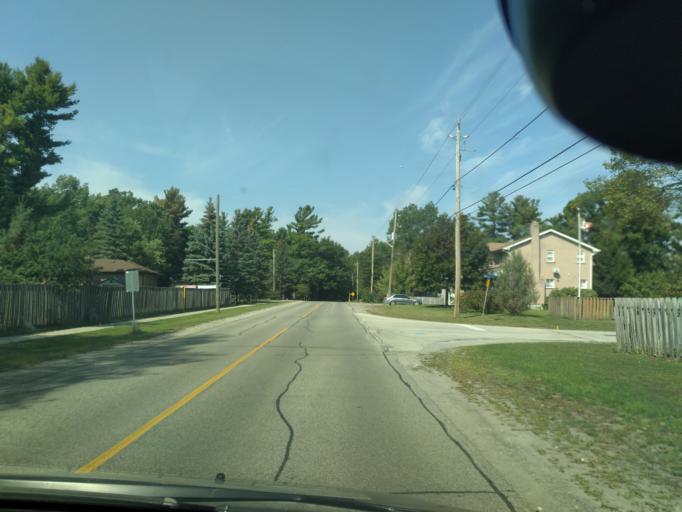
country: CA
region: Ontario
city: Newmarket
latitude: 44.1205
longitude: -79.5062
